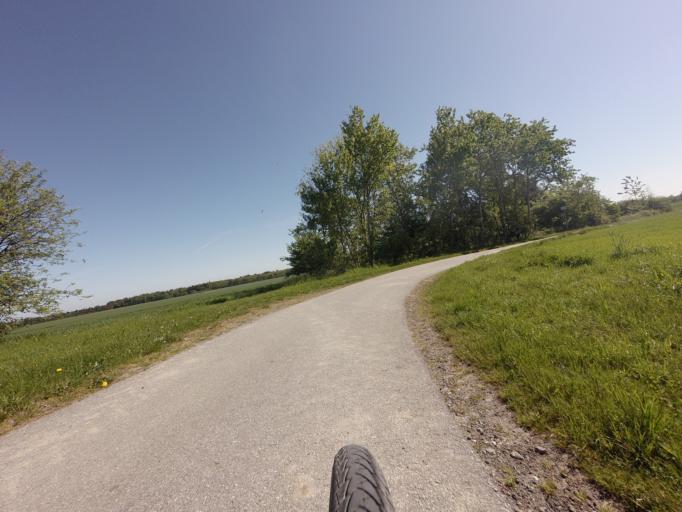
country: DK
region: North Denmark
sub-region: Hjorring Kommune
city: Vra
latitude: 57.3805
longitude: 9.8172
